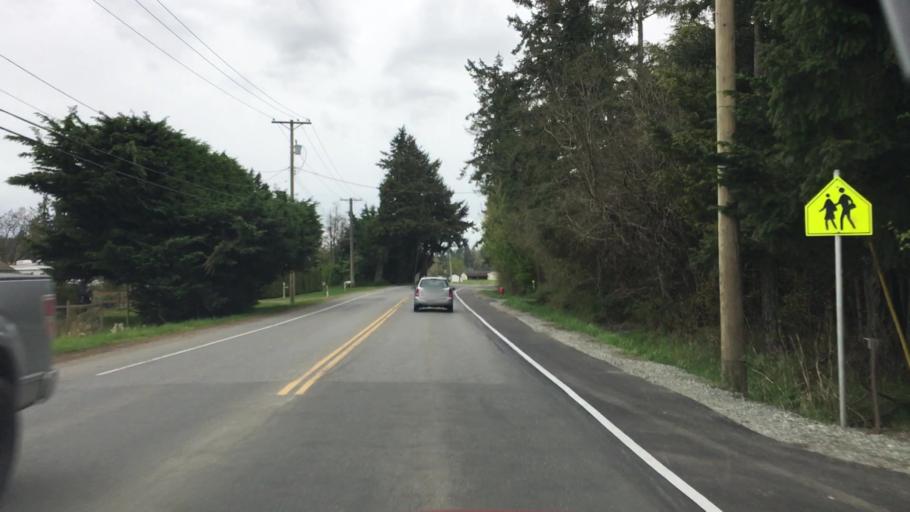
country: CA
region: British Columbia
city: North Saanich
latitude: 48.5706
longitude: -123.4415
